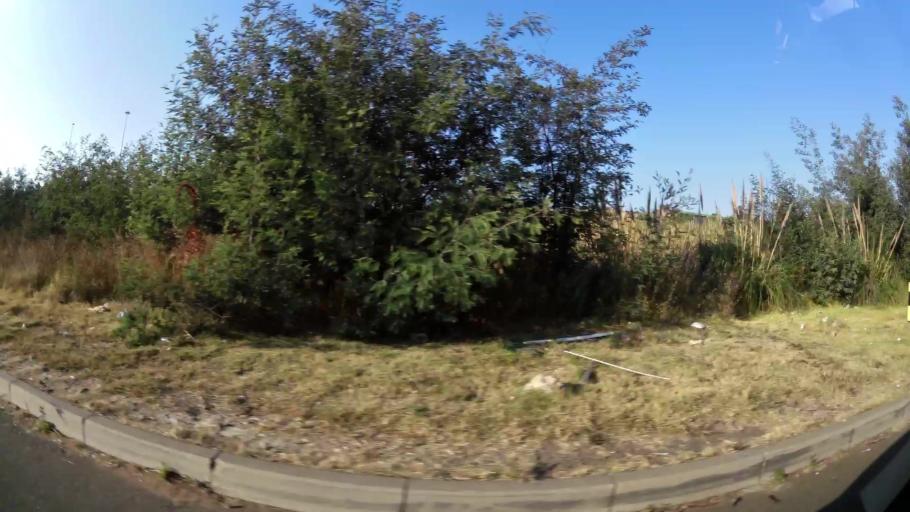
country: ZA
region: Gauteng
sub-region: City of Johannesburg Metropolitan Municipality
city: Modderfontein
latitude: -26.1534
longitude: 28.1869
